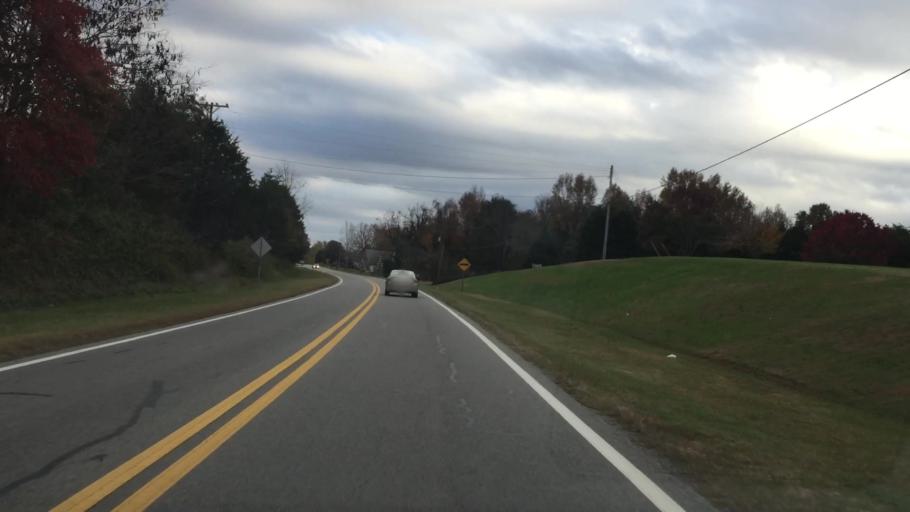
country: US
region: North Carolina
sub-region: Rockingham County
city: Reidsville
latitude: 36.2849
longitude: -79.6034
